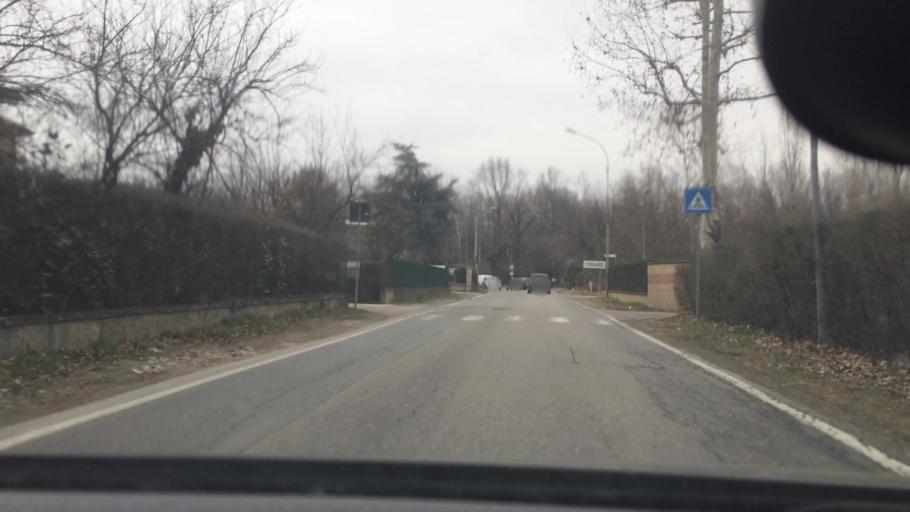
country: IT
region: Lombardy
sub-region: Provincia di Monza e Brianza
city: Villaggio del Sole
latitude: 45.6381
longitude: 9.1093
